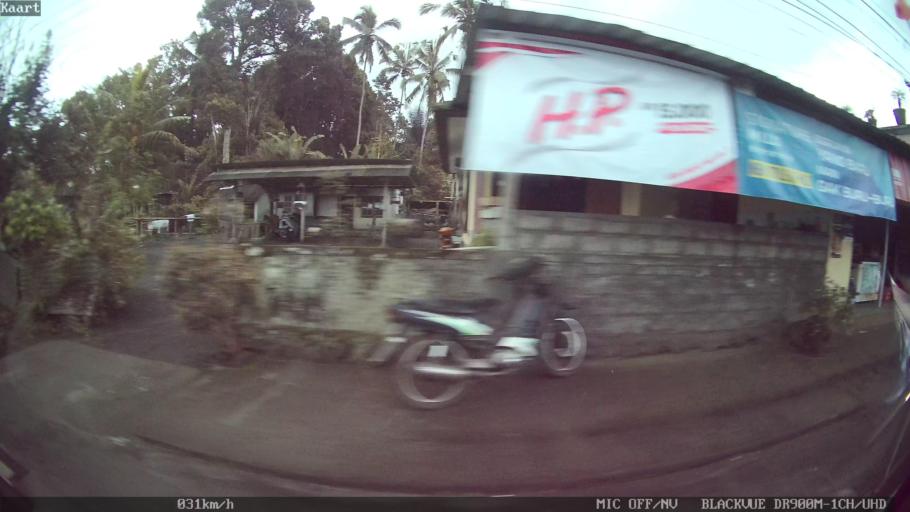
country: ID
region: Bali
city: Banjar Kubu
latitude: -8.4285
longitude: 115.4245
